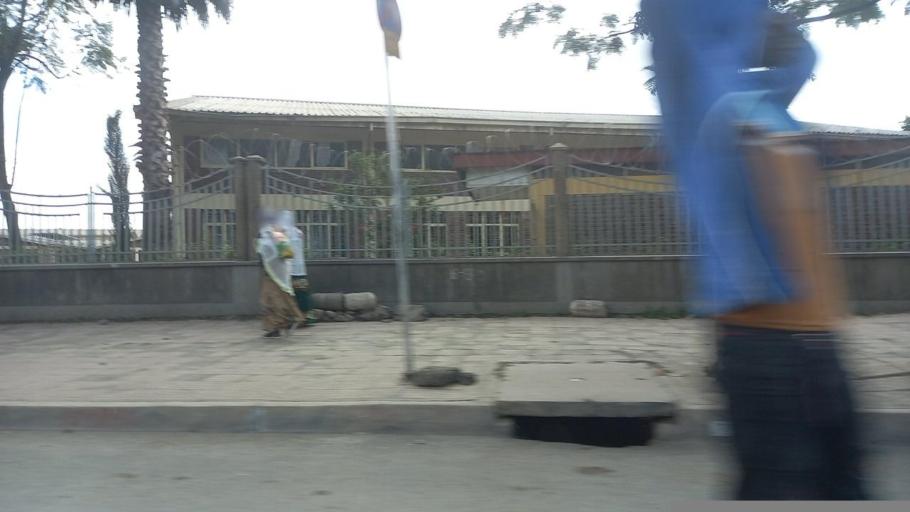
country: ET
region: Adis Abeba
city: Addis Ababa
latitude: 8.9617
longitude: 38.7163
